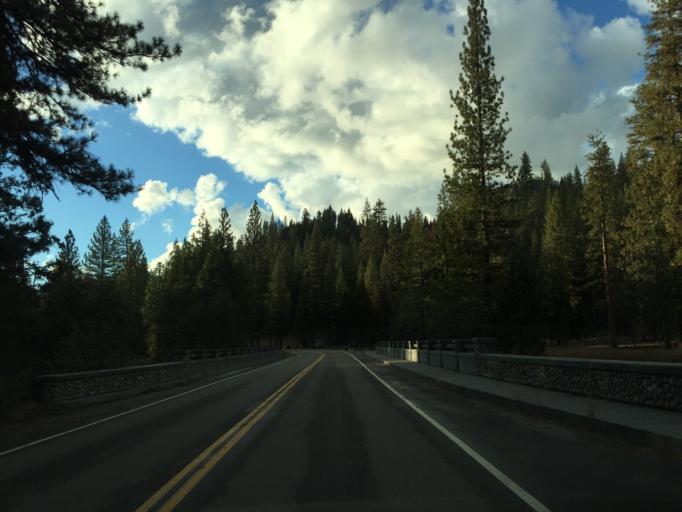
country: US
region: California
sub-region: Madera County
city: Ahwahnee
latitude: 37.5381
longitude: -119.6587
